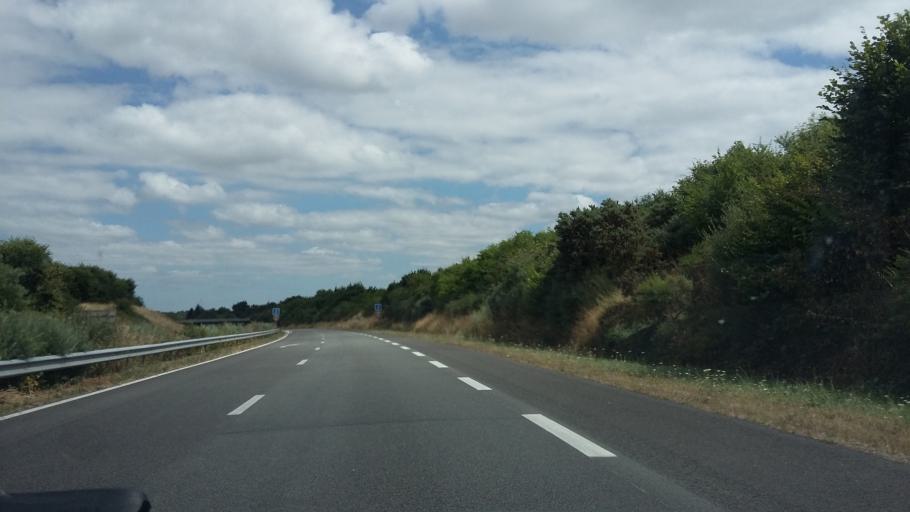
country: FR
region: Pays de la Loire
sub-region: Departement de la Vendee
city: Bournezeau
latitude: 46.6308
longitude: -1.1765
